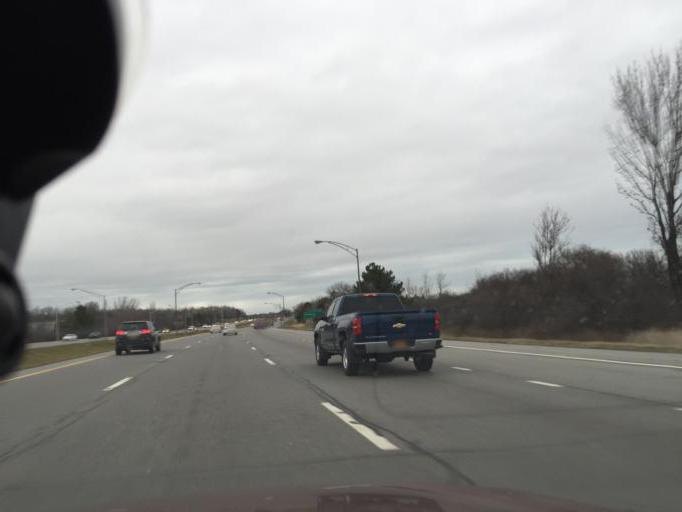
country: US
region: New York
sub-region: Monroe County
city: North Gates
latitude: 43.1826
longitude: -77.6837
